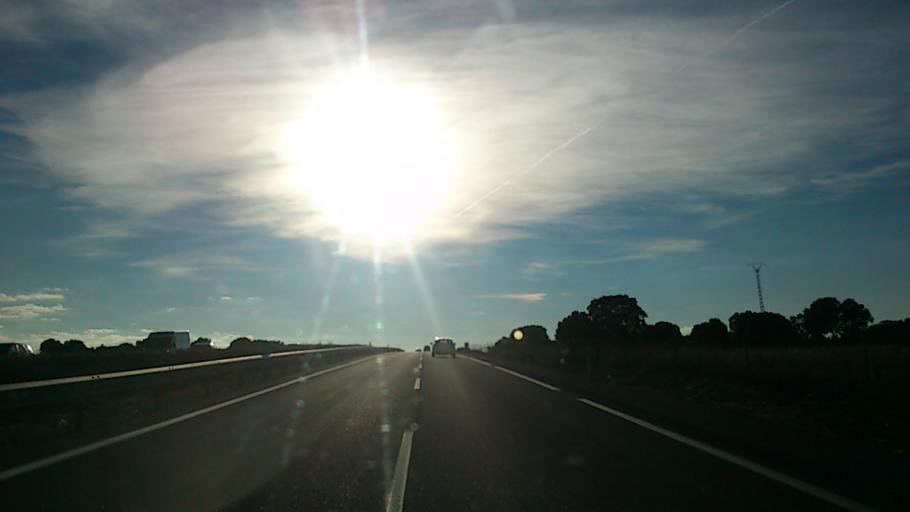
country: ES
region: Castille-La Mancha
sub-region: Provincia de Guadalajara
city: Mirabueno
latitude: 40.9425
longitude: -2.6972
